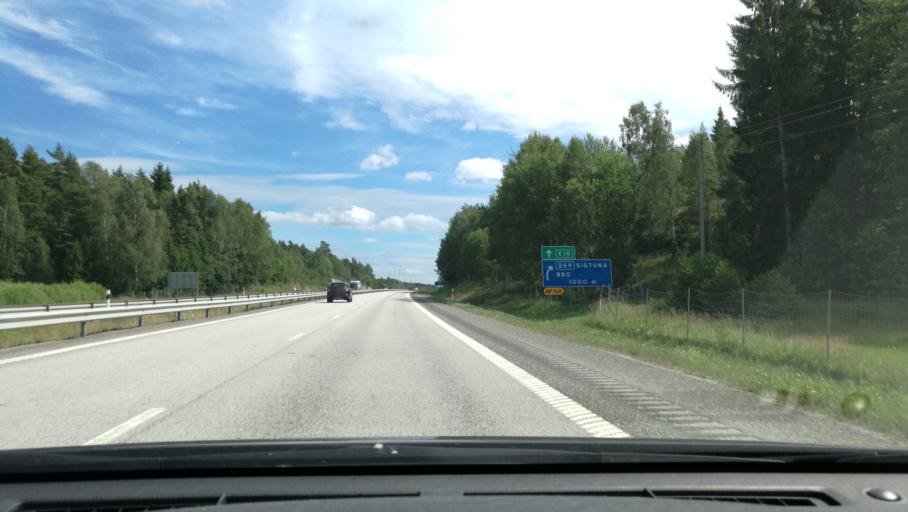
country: SE
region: Stockholm
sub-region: Upplands-Bro Kommun
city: Bro
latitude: 59.5389
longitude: 17.6170
